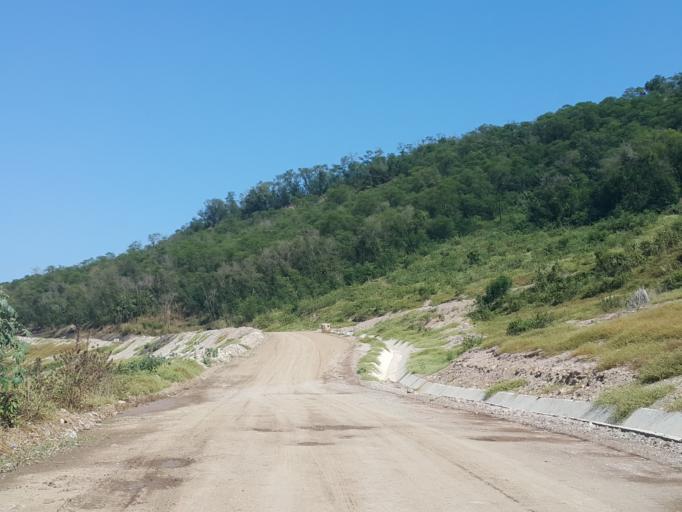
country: TH
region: Lampang
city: Mae Mo
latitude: 18.3221
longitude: 99.7372
